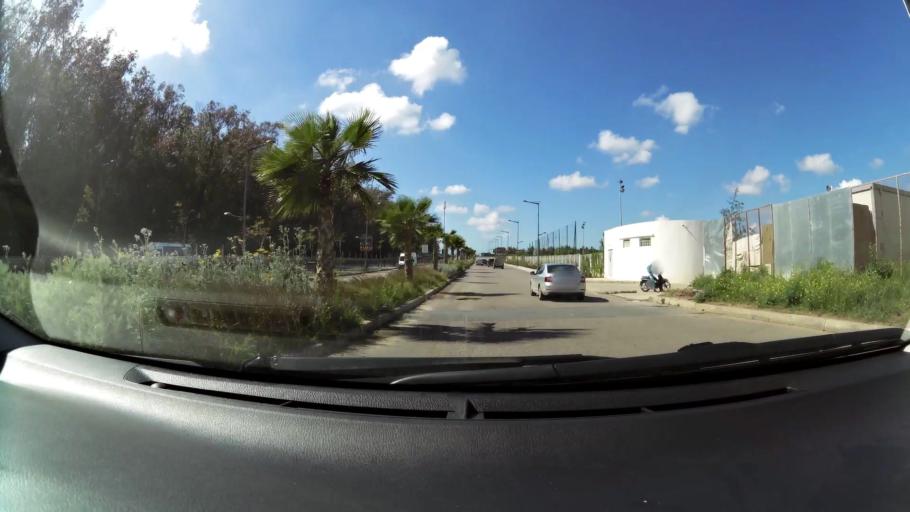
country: MA
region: Grand Casablanca
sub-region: Nouaceur
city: Bouskoura
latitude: 33.4775
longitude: -7.6211
